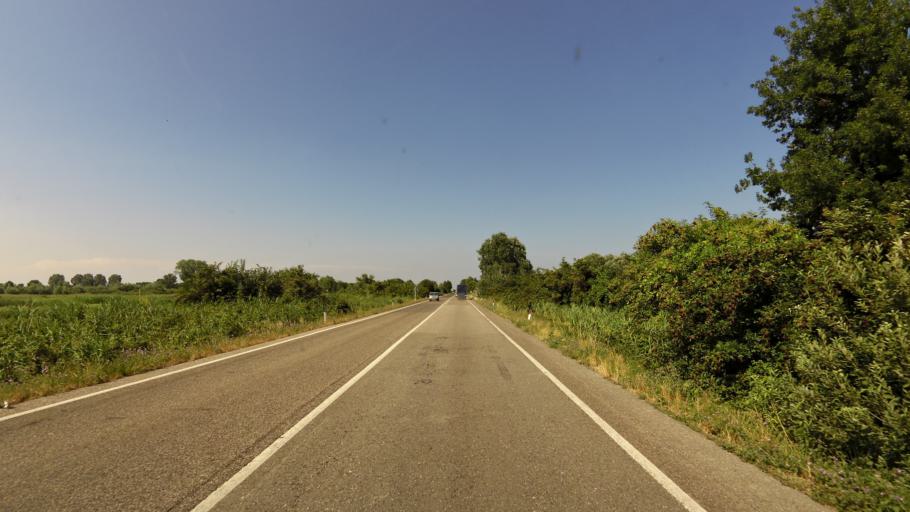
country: IT
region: Emilia-Romagna
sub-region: Provincia di Ravenna
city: Marina Romea
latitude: 44.5417
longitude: 12.2355
